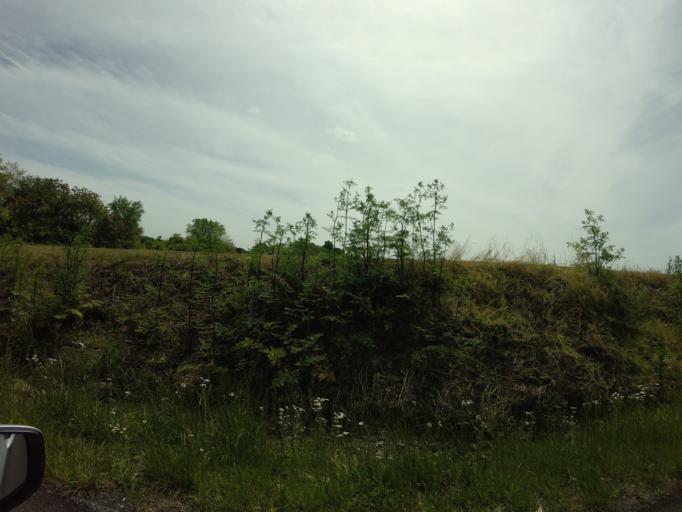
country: US
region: Maryland
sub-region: Frederick County
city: Linganore
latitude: 39.4975
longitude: -77.1962
